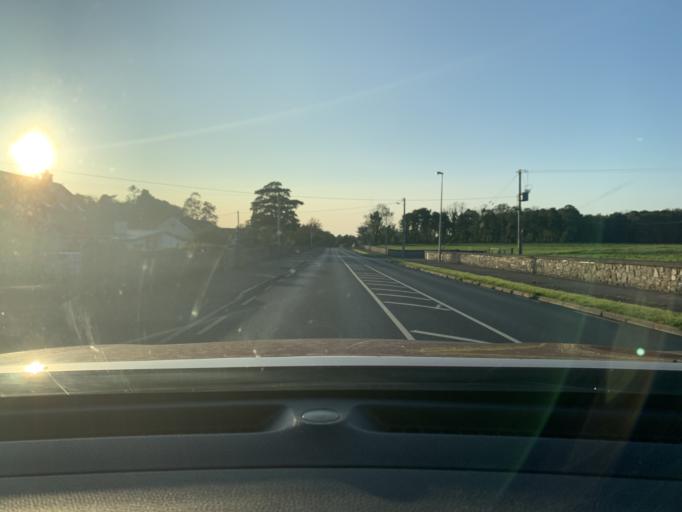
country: IE
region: Connaught
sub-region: Sligo
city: Sligo
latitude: 54.2709
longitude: -8.4232
